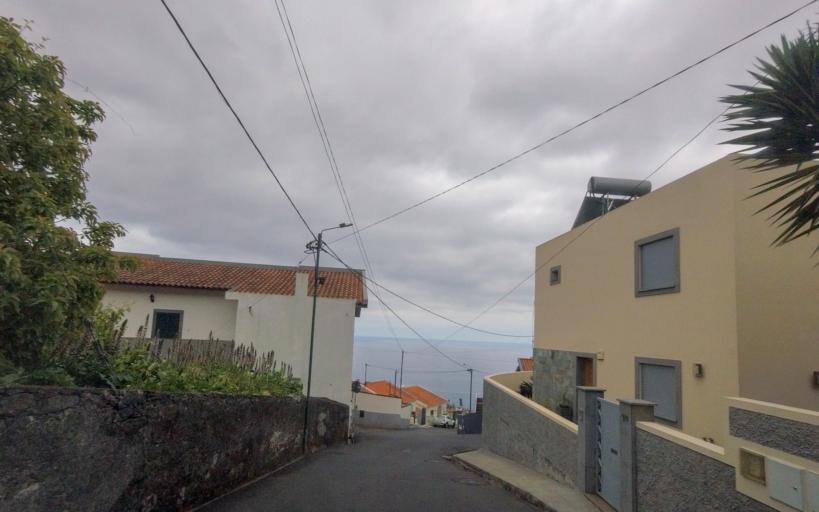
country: PT
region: Madeira
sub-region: Funchal
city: Nossa Senhora do Monte
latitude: 32.6584
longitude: -16.8806
